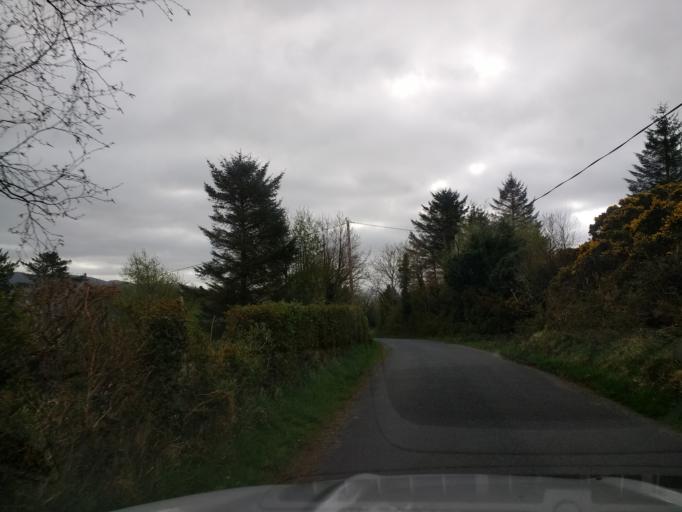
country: IE
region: Ulster
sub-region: County Donegal
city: Buncrana
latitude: 55.2225
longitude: -7.6129
